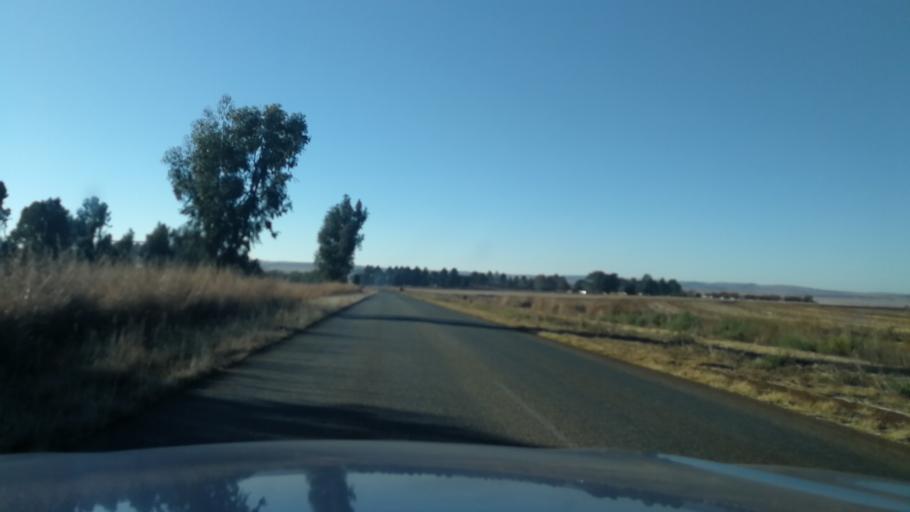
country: ZA
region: North-West
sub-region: Bojanala Platinum District Municipality
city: Rustenburg
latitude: -25.9687
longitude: 27.2251
